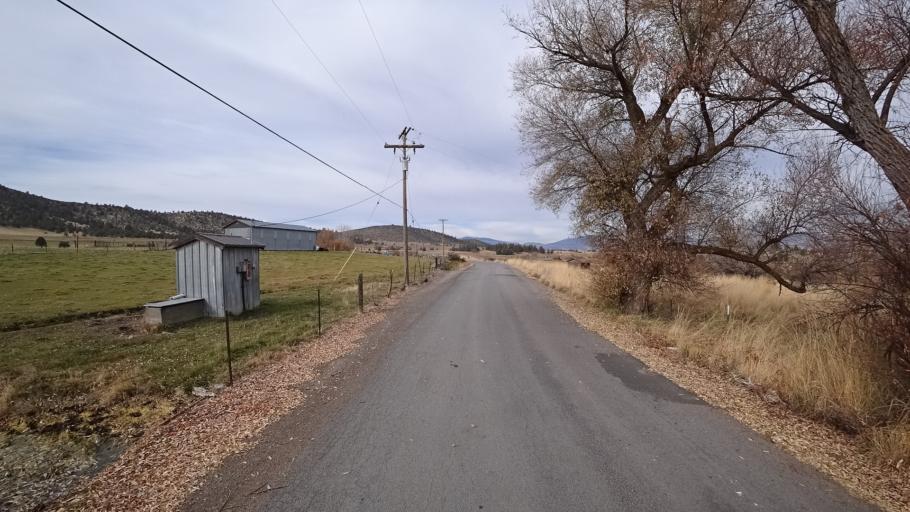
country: US
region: California
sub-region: Siskiyou County
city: Montague
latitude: 41.6829
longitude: -122.5277
